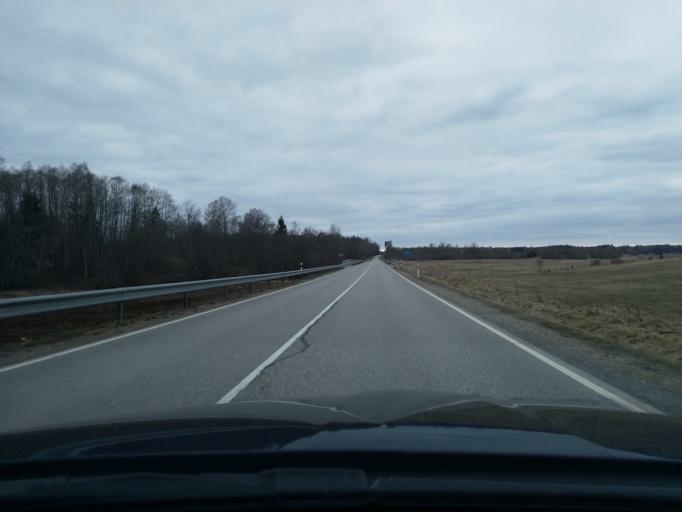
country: LV
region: Kuldigas Rajons
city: Kuldiga
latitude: 56.9661
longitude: 22.0602
